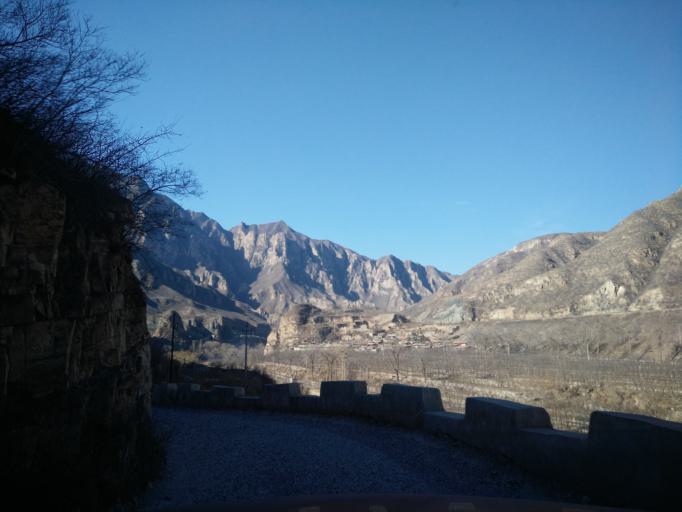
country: CN
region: Beijing
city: Yanjiatai
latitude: 40.1681
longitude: 115.6608
